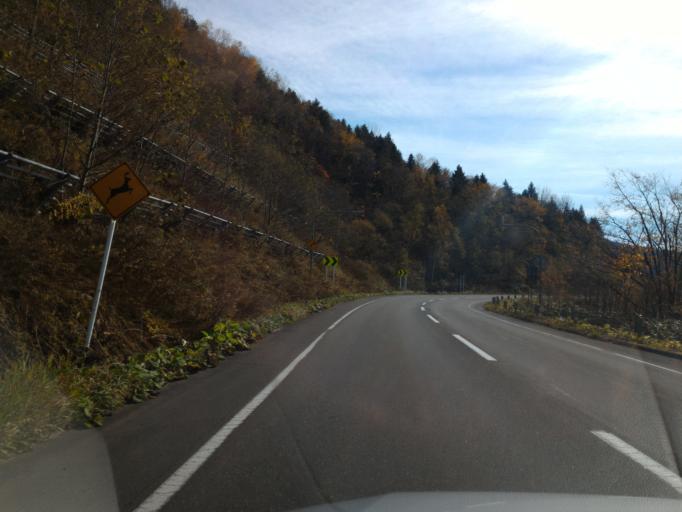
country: JP
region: Hokkaido
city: Shimo-furano
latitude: 43.3612
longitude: 142.2420
